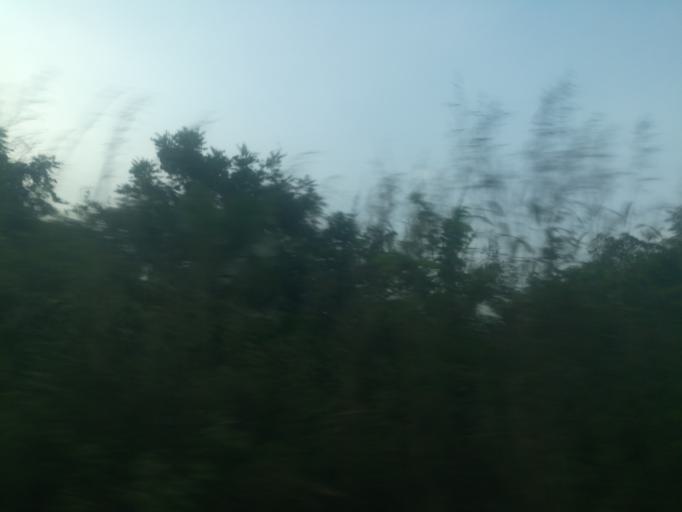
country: NG
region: Ogun
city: Abeokuta
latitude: 7.1498
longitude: 3.2592
